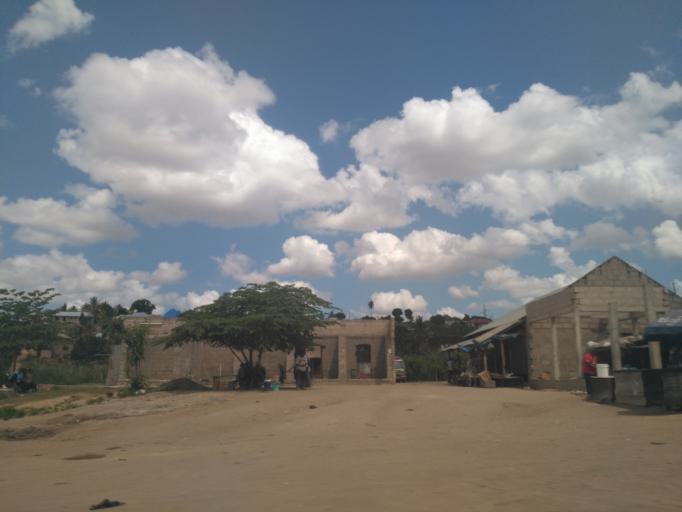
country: TZ
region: Dar es Salaam
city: Dar es Salaam
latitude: -6.9049
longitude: 39.2381
